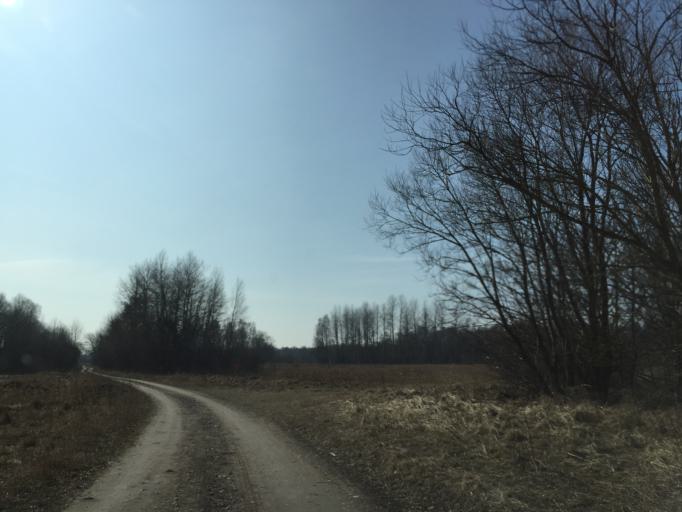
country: LV
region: Dundaga
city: Dundaga
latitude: 57.9327
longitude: 22.0644
